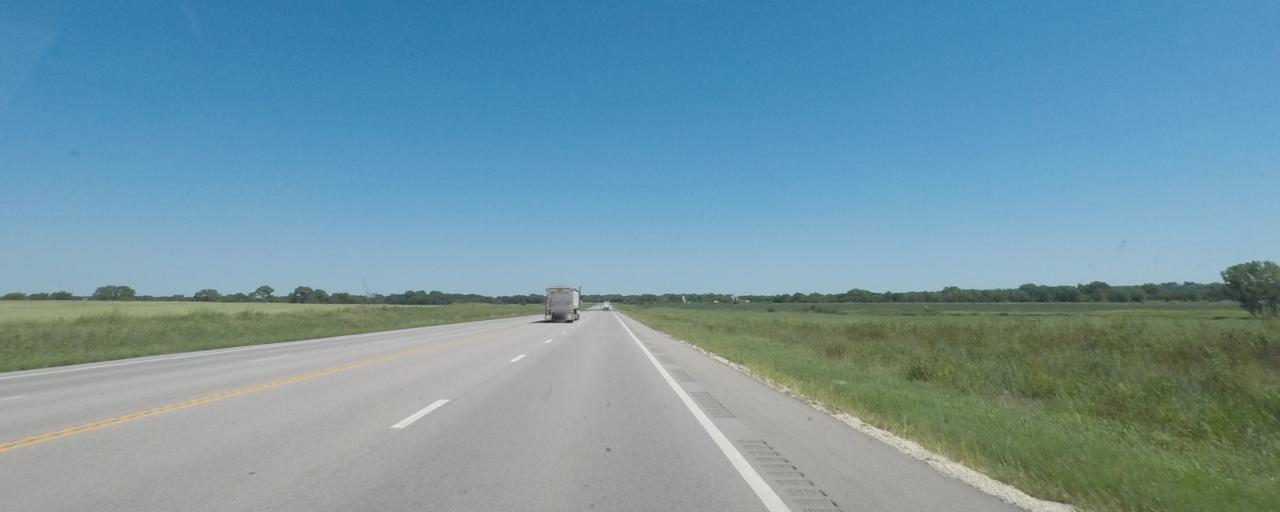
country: US
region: Kansas
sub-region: Chase County
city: Cottonwood Falls
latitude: 38.4053
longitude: -96.4086
